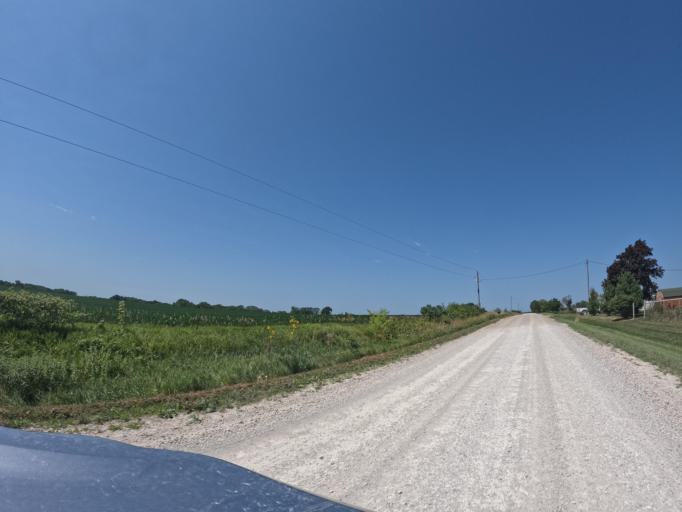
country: US
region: Iowa
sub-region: Henry County
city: Mount Pleasant
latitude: 40.8893
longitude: -91.5876
